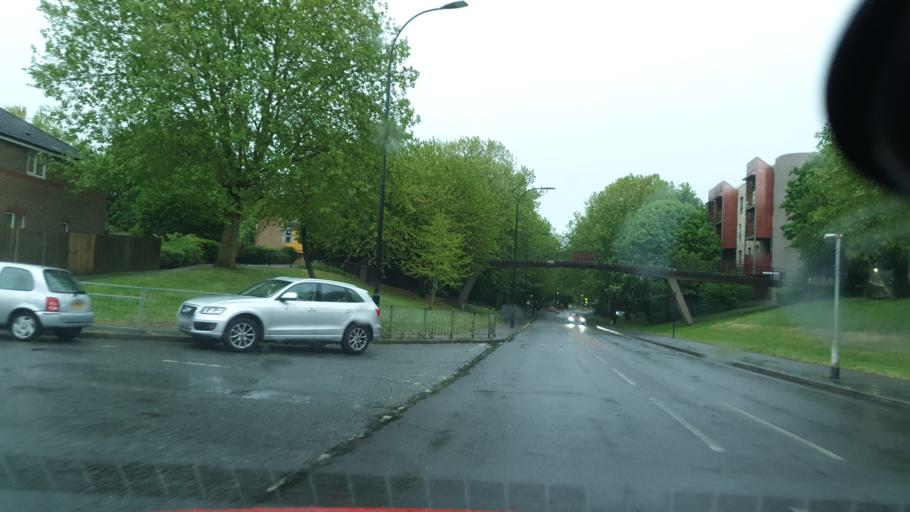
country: GB
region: England
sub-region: Greater London
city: Poplar
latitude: 51.5020
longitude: -0.0356
